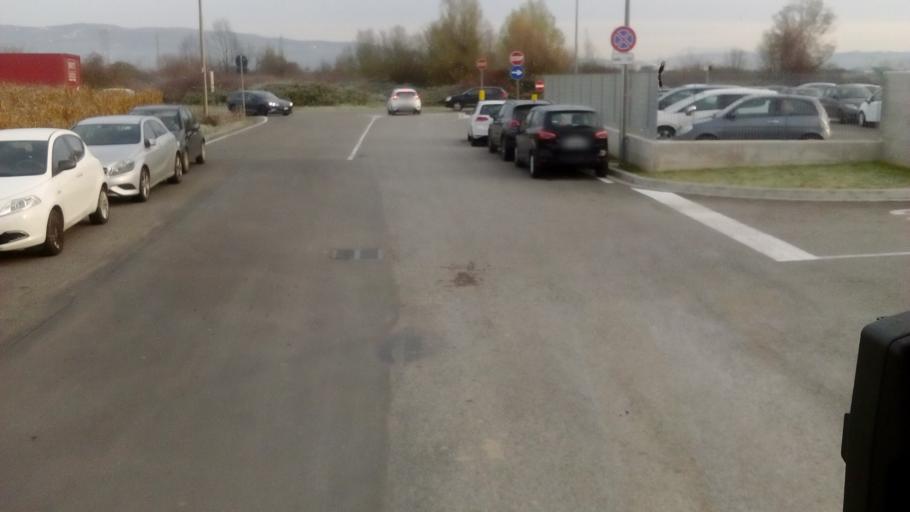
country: IT
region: Tuscany
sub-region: Province of Florence
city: Pozzale-Case Nuove
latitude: 43.7116
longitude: 10.9759
